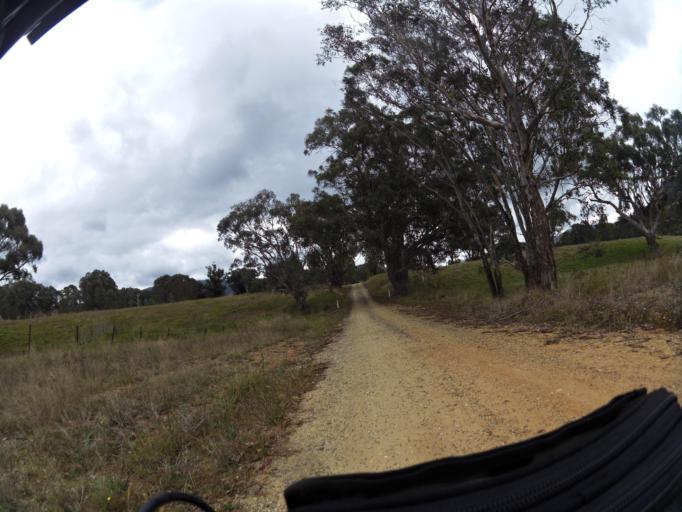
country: AU
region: New South Wales
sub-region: Albury Municipality
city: East Albury
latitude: -36.1919
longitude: 147.3345
